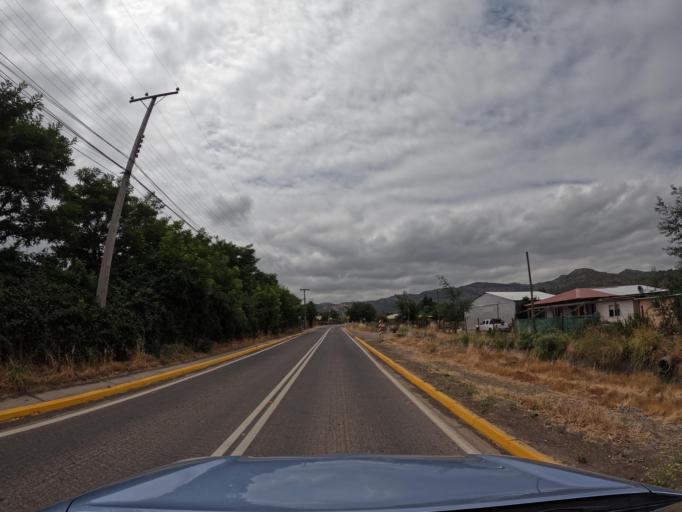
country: CL
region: Maule
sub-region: Provincia de Curico
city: Teno
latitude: -34.7741
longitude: -71.1845
